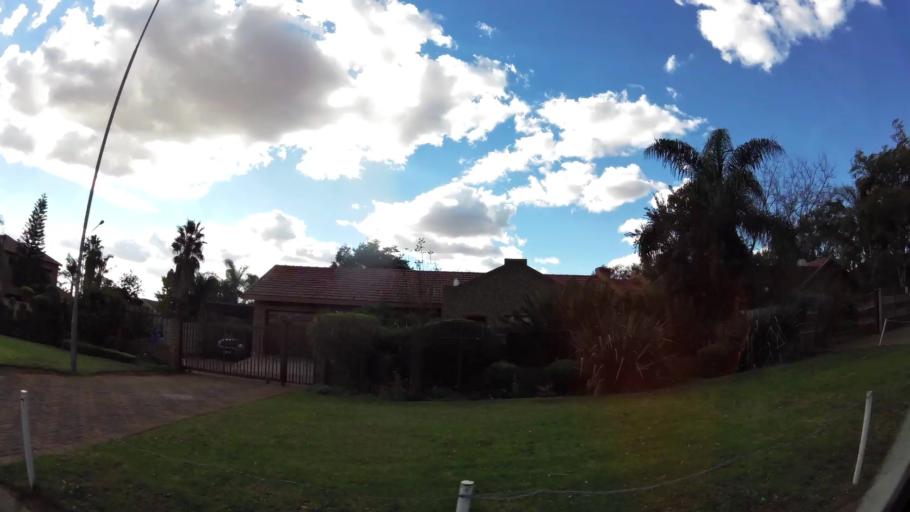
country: ZA
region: Limpopo
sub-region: Capricorn District Municipality
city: Polokwane
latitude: -23.9122
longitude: 29.4988
